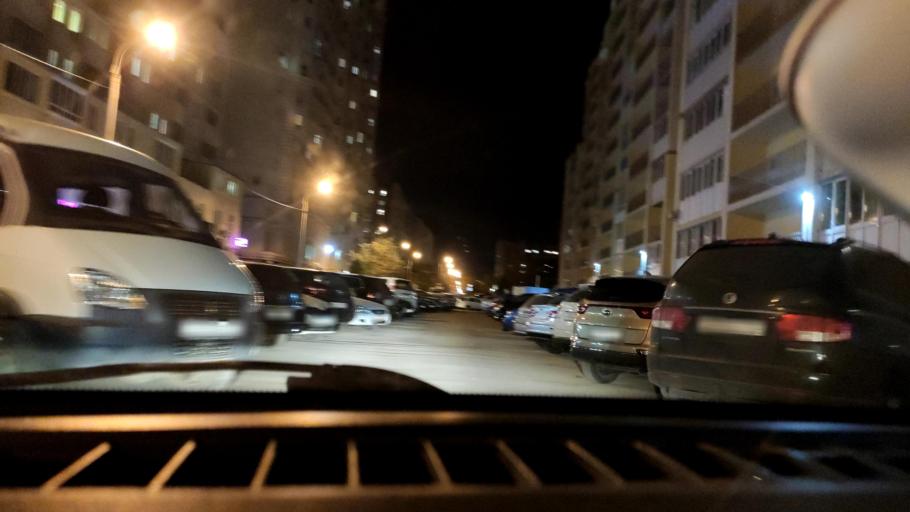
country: RU
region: Samara
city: Samara
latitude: 53.2224
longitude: 50.1929
